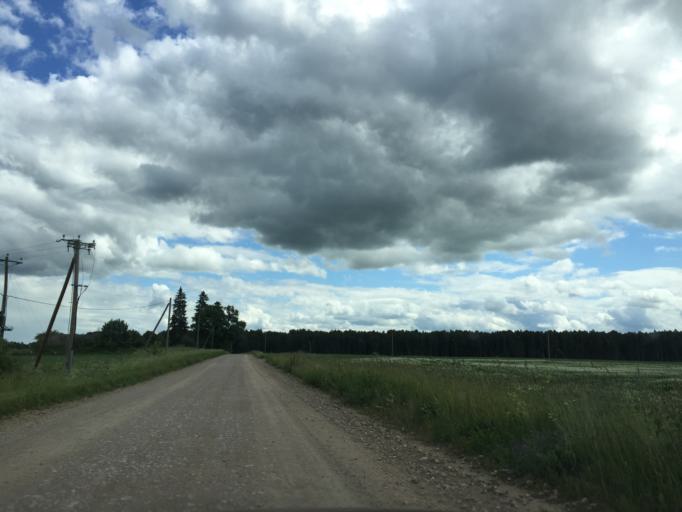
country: LV
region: Vecumnieki
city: Vecumnieki
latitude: 56.4702
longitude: 24.4226
